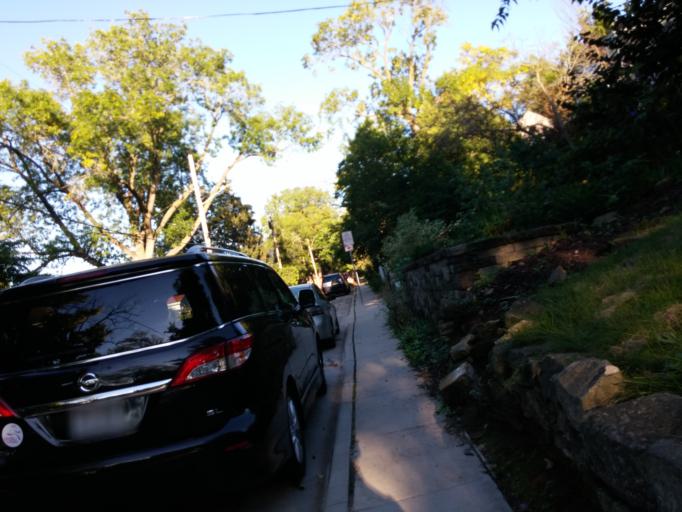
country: US
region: Wisconsin
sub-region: Dane County
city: Shorewood Hills
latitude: 43.0701
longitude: -89.4285
